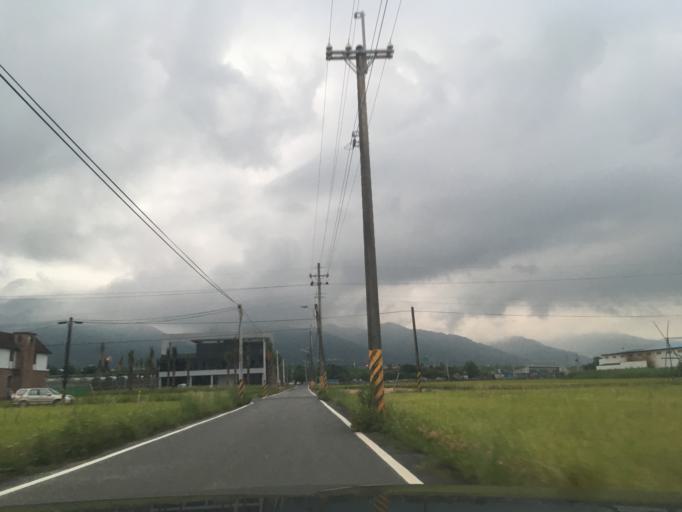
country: TW
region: Taiwan
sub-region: Yilan
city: Yilan
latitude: 24.8190
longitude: 121.7866
